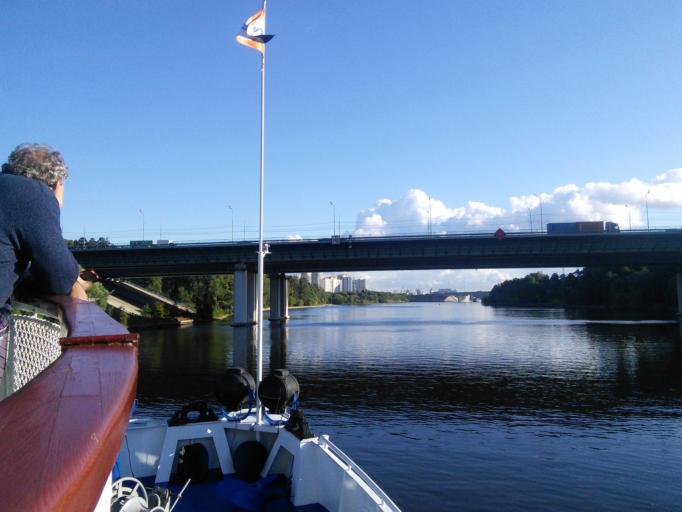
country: RU
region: Moskovskaya
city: Levoberezhnaya
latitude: 55.8841
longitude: 37.4582
